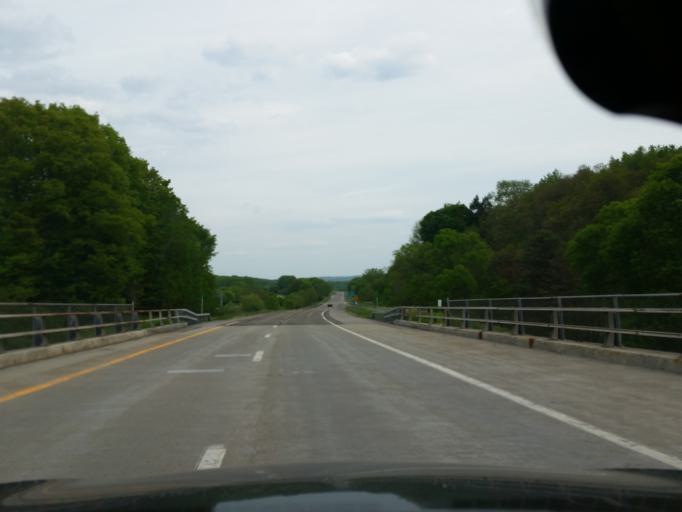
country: US
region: New York
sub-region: Chautauqua County
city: Lakewood
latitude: 42.1678
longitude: -79.3857
